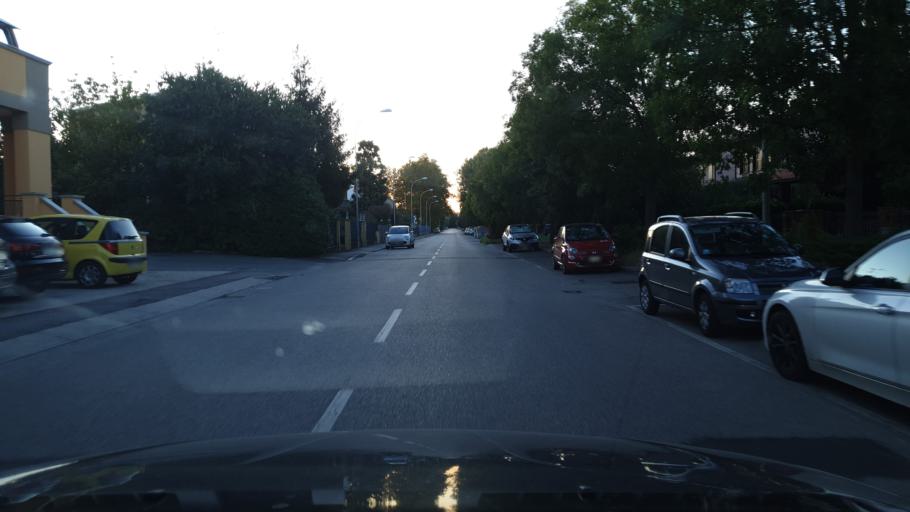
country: IT
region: Emilia-Romagna
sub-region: Provincia di Bologna
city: Quarto Inferiore
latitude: 44.5496
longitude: 11.3987
